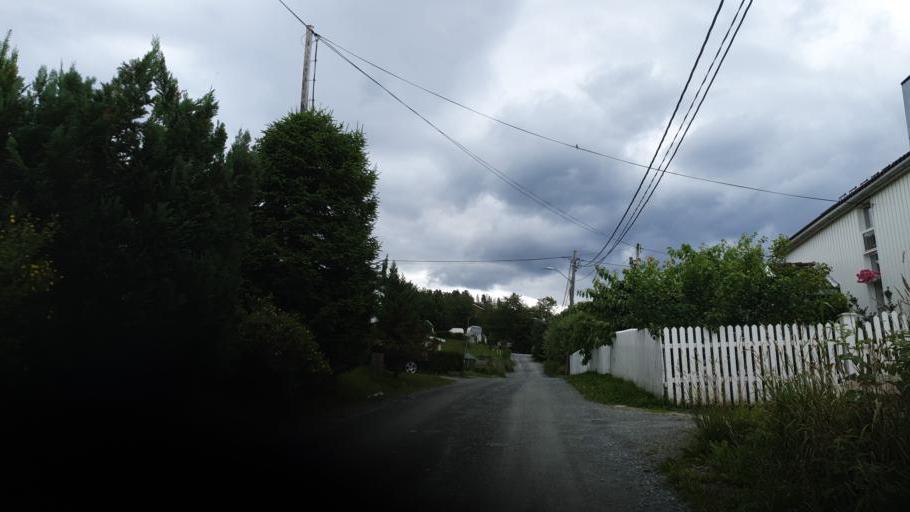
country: NO
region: Sor-Trondelag
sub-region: Malvik
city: Malvik
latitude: 63.4405
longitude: 10.5979
